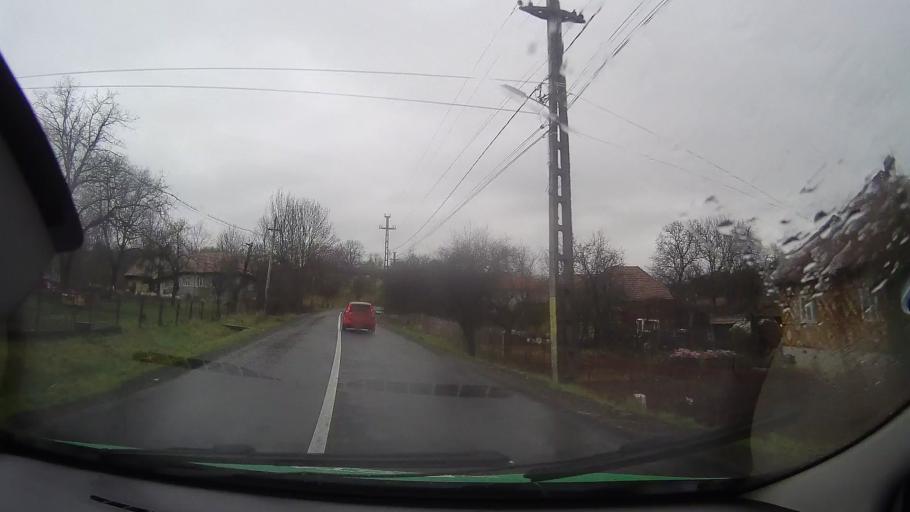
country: RO
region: Mures
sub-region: Comuna Vatava
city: Vatava
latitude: 46.9474
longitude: 24.7620
